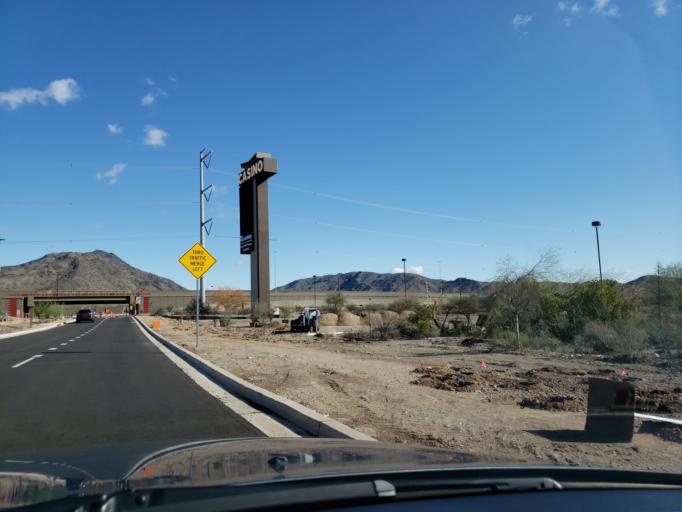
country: US
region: Arizona
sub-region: Maricopa County
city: Laveen
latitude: 33.3142
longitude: -112.1597
